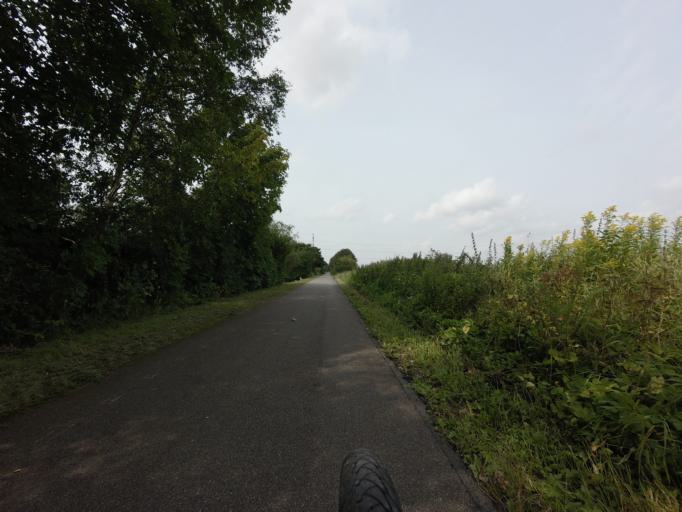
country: DK
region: Zealand
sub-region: Naestved Kommune
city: Naestved
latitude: 55.2527
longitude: 11.7162
